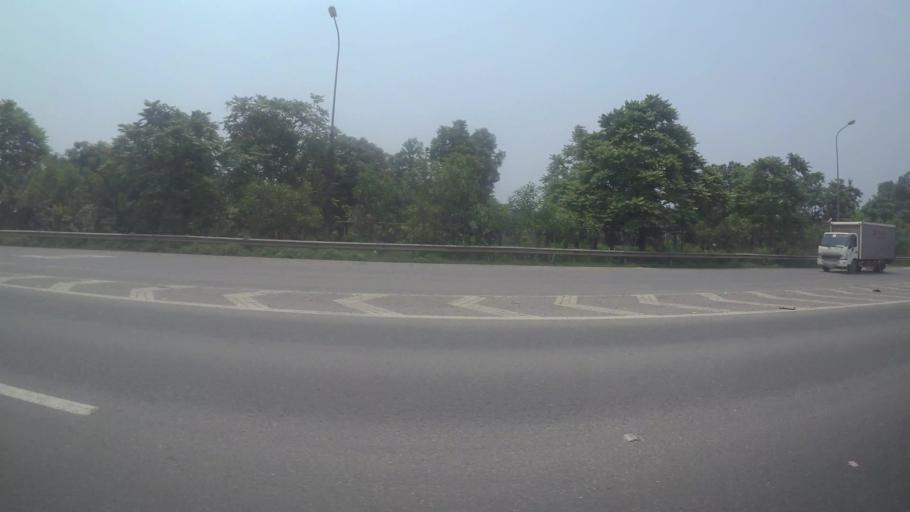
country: VN
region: Ha Noi
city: Lien Quan
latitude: 20.9903
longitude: 105.5431
